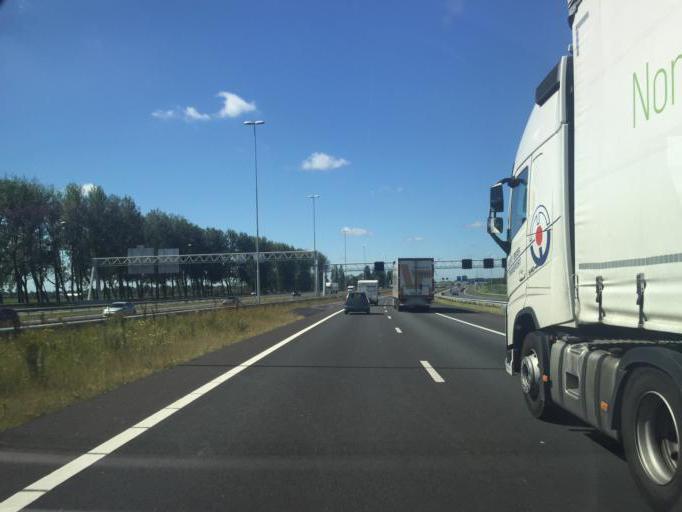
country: NL
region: South Holland
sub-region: Gemeente Leiden
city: Leiden
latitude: 52.1379
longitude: 4.5065
